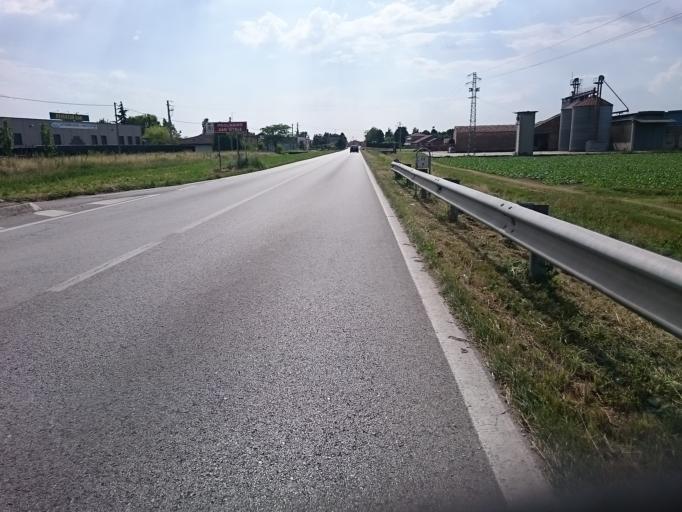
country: IT
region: Veneto
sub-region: Provincia di Padova
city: Megliadino San Vitale
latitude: 45.1953
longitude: 11.5067
